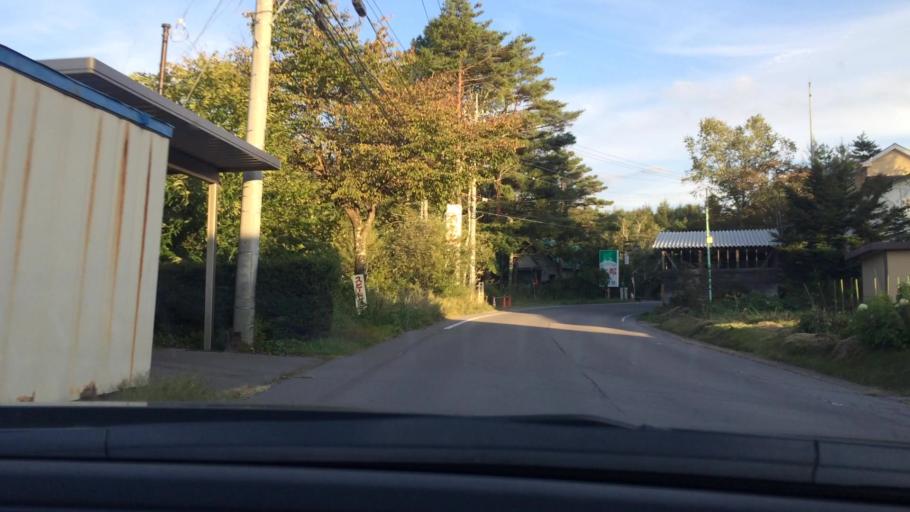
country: JP
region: Nagano
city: Komoro
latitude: 36.4868
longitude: 138.5164
